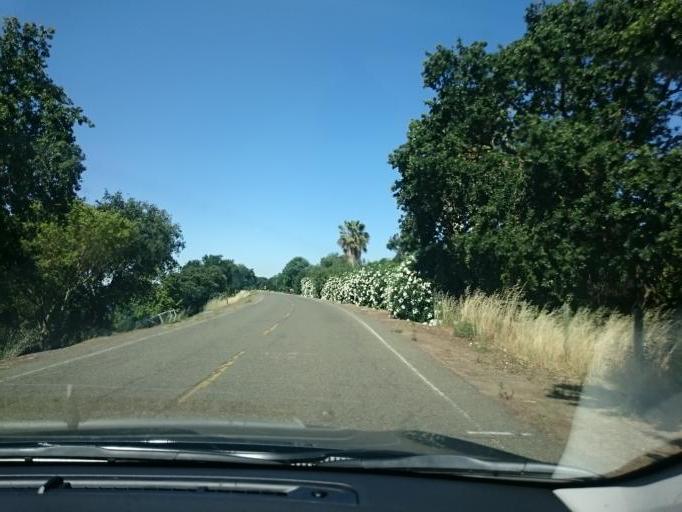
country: US
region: California
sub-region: Yolo County
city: West Sacramento
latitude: 38.5166
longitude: -121.5466
